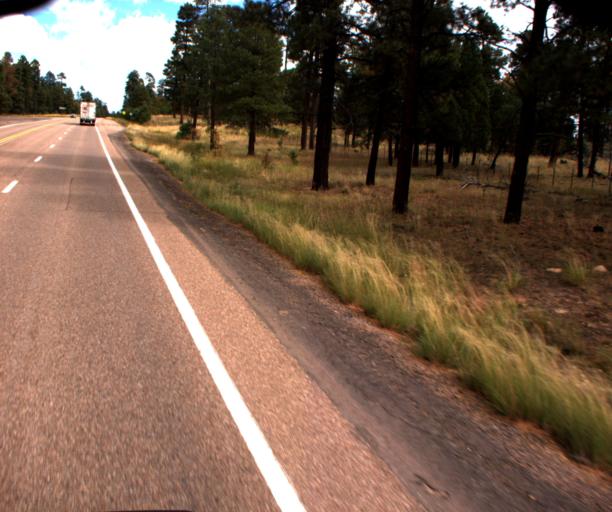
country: US
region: Arizona
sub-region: Navajo County
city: Heber-Overgaard
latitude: 34.3657
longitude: -110.6890
